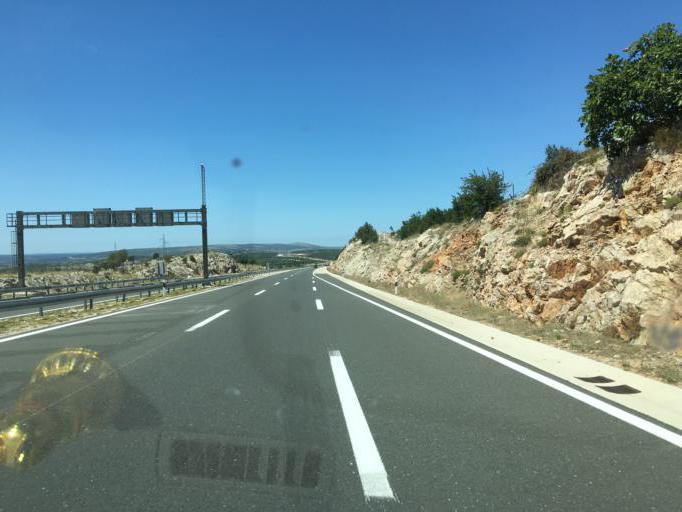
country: HR
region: Zadarska
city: Krusevo
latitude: 44.2386
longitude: 15.5999
